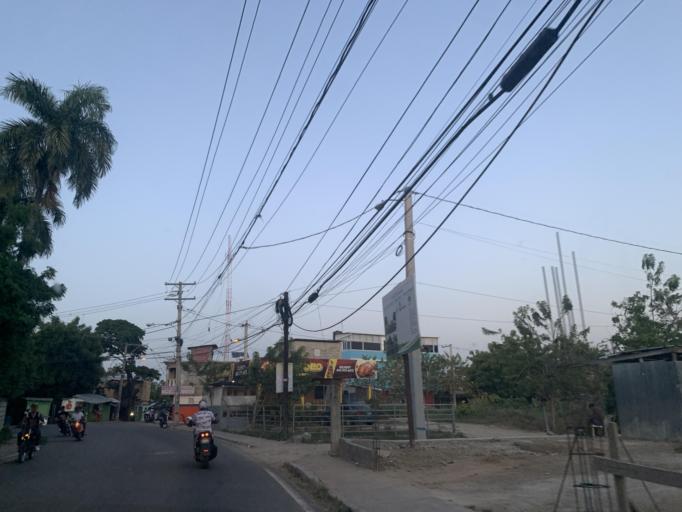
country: DO
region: Puerto Plata
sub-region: Puerto Plata
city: Puerto Plata
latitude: 19.8038
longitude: -70.7165
